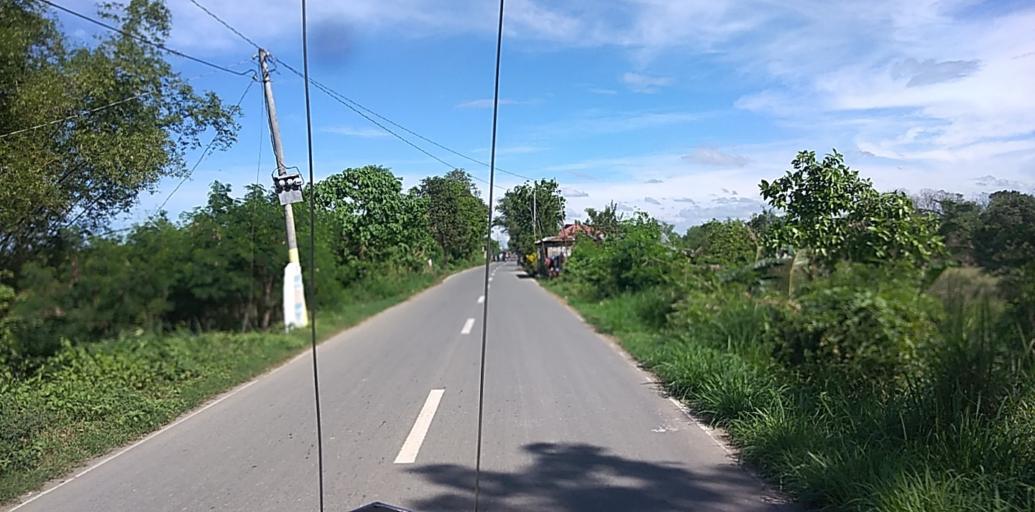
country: PH
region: Central Luzon
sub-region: Province of Pampanga
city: Candaba
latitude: 15.1020
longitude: 120.8148
